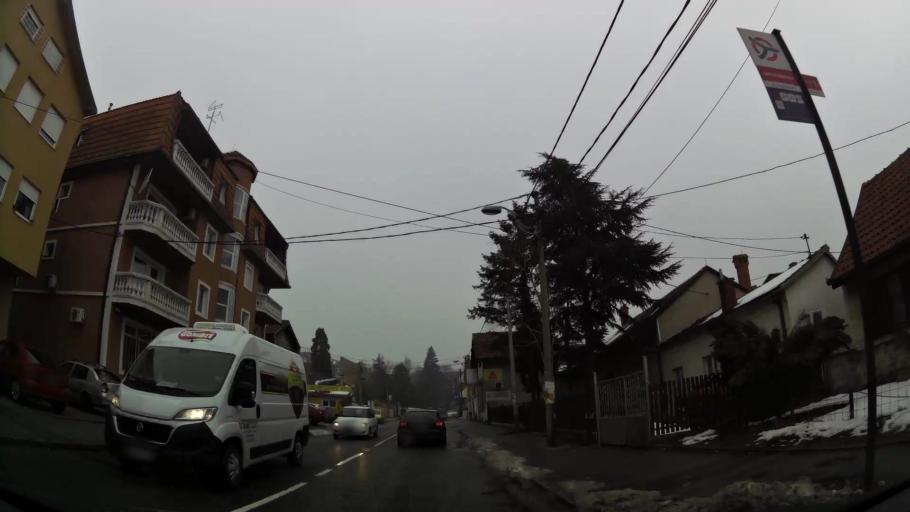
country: RS
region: Central Serbia
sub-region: Belgrade
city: Vozdovac
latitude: 44.7791
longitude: 20.4797
